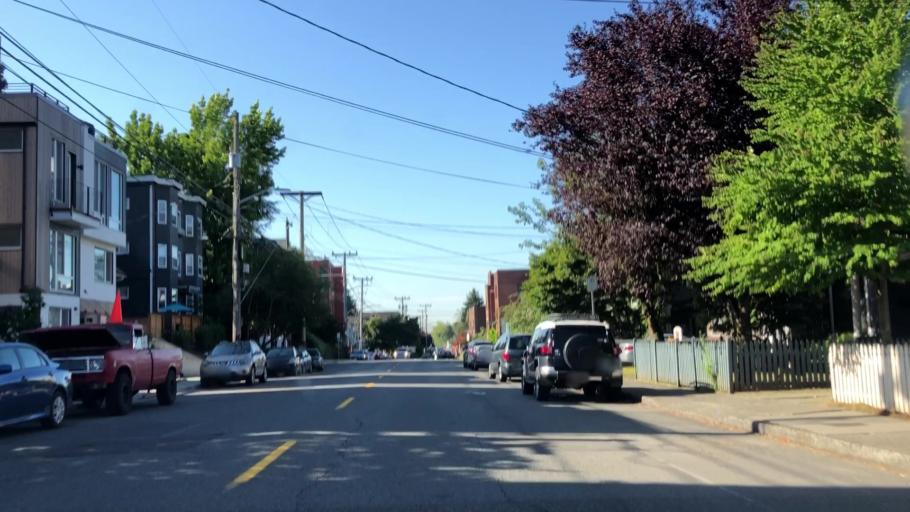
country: US
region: Washington
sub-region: King County
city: Seattle
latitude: 47.6226
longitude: -122.3168
